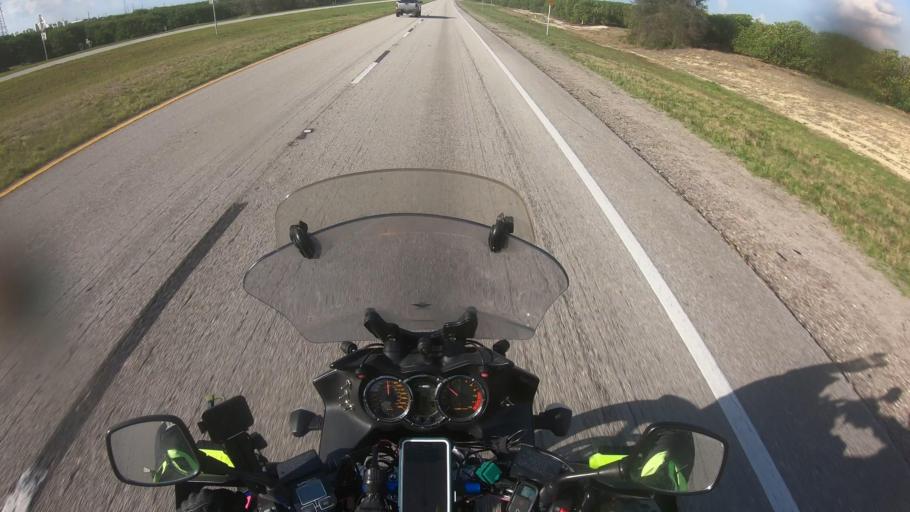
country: US
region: Florida
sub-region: Highlands County
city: Placid Lakes
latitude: 27.2029
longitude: -81.3281
